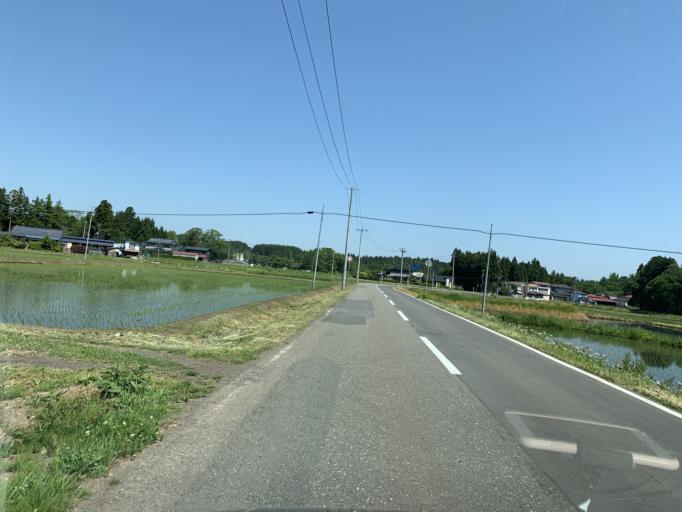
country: JP
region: Iwate
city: Mizusawa
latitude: 39.1705
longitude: 141.0609
